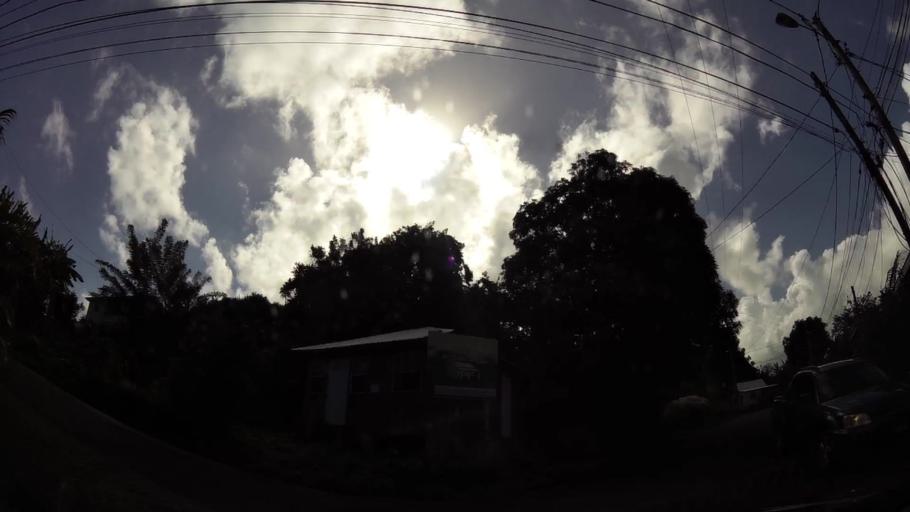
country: DM
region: Saint Andrew
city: Marigot
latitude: 15.5404
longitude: -61.2834
